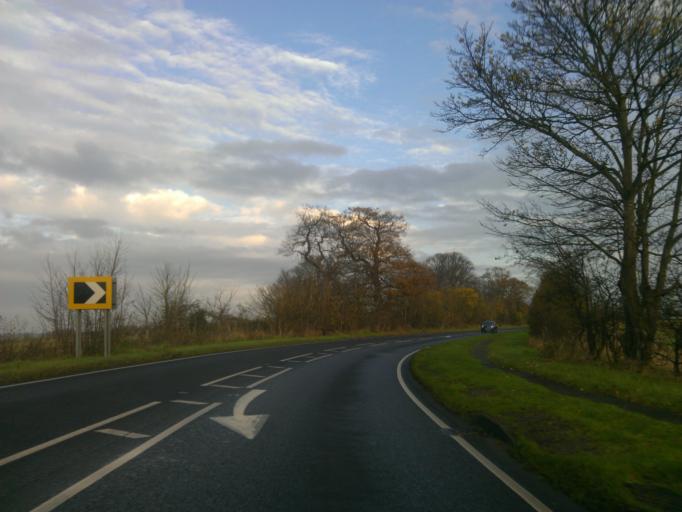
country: GB
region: England
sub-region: Essex
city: Saint Osyth
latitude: 51.8095
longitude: 1.0733
